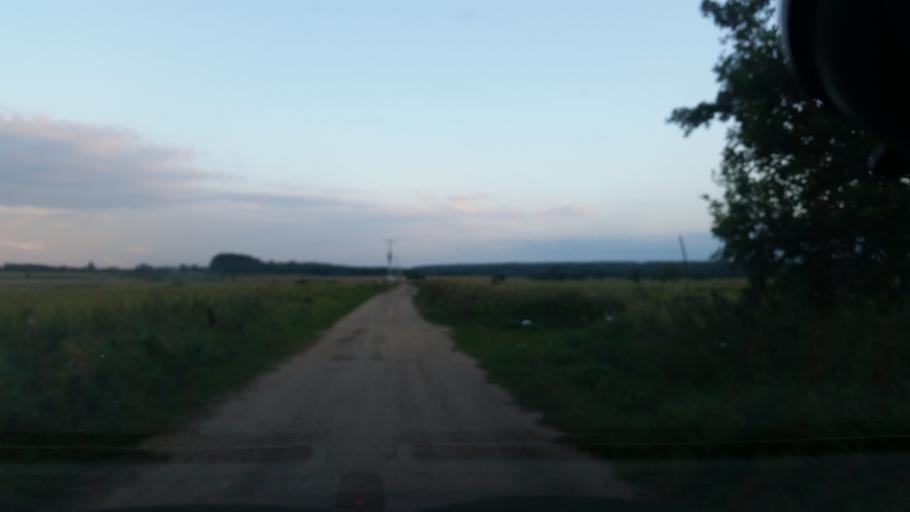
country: PL
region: Pomeranian Voivodeship
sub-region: Powiat wejherowski
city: Choczewo
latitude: 54.7821
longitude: 17.7934
